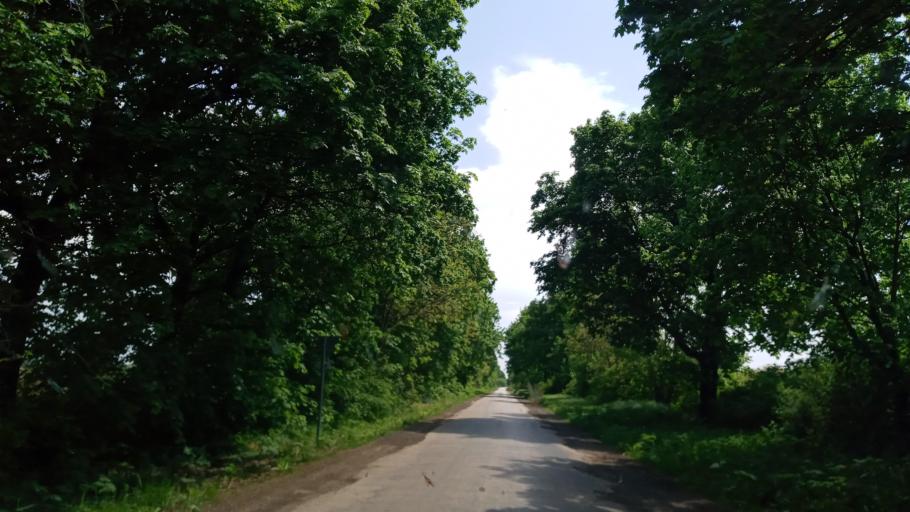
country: HU
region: Baranya
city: Villany
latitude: 45.8331
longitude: 18.4999
